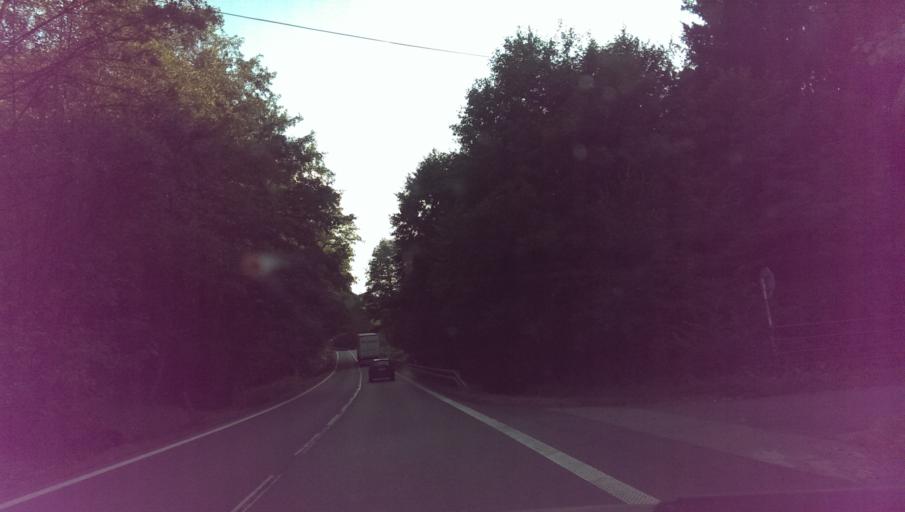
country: CZ
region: Zlin
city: Slusovice
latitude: 49.2060
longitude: 17.8054
